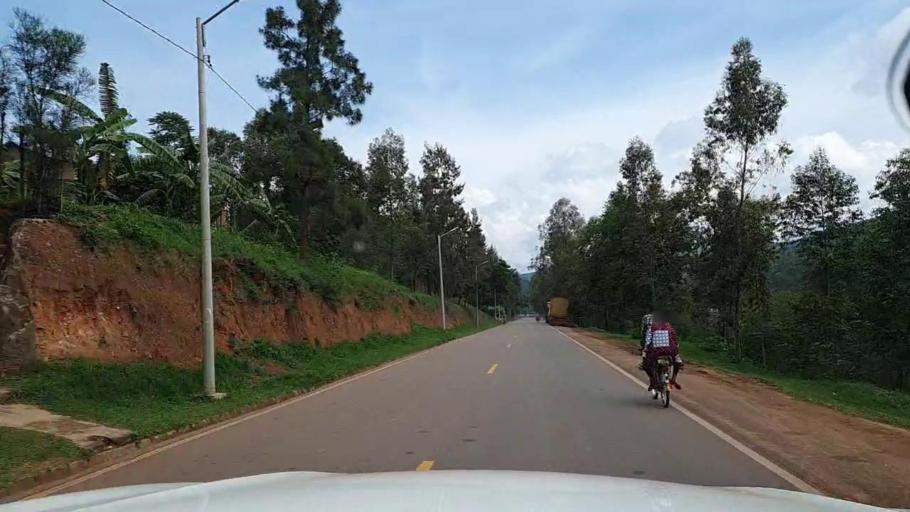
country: RW
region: Kigali
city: Kigali
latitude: -1.8711
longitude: 30.0837
